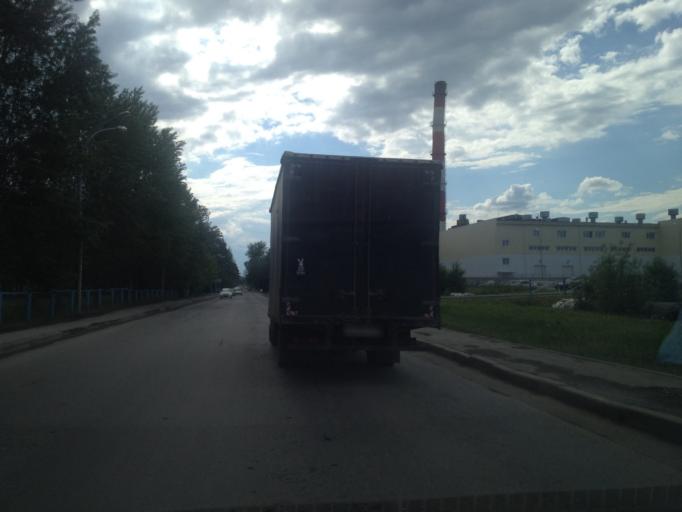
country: RU
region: Sverdlovsk
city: Sovkhoznyy
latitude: 56.7645
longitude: 60.5903
